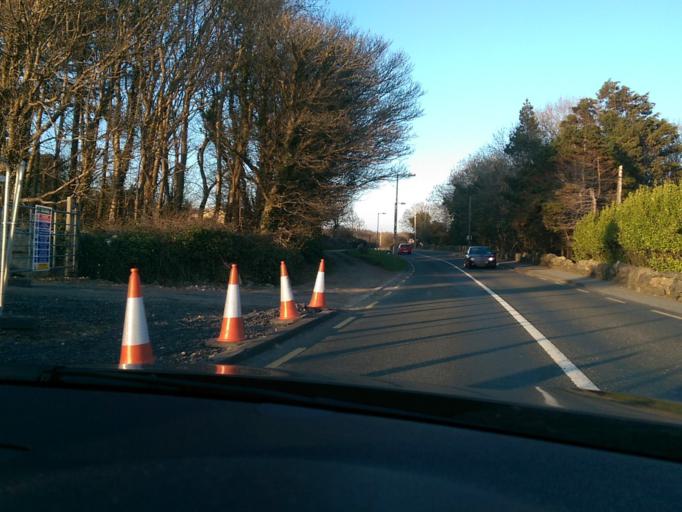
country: IE
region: Connaught
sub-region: County Galway
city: Bearna
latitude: 53.2533
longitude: -9.1369
